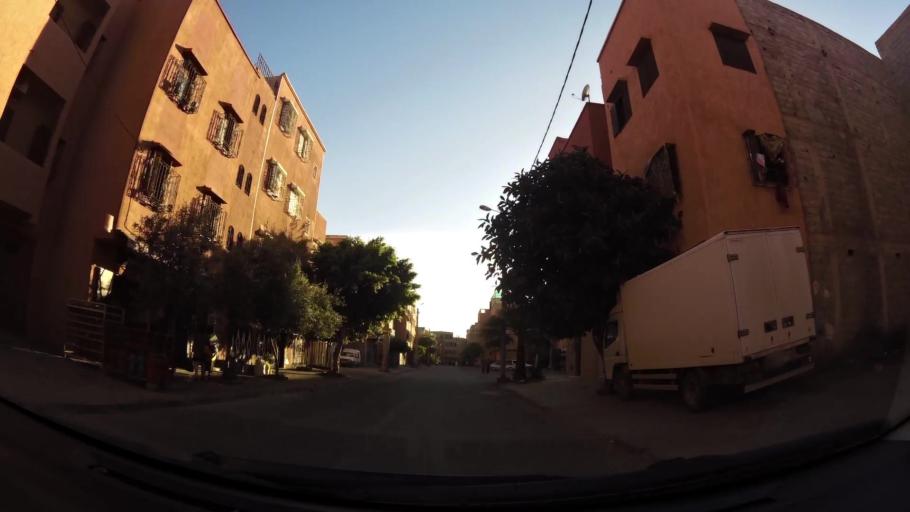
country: MA
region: Marrakech-Tensift-Al Haouz
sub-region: Marrakech
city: Marrakesh
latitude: 31.6172
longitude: -8.0533
